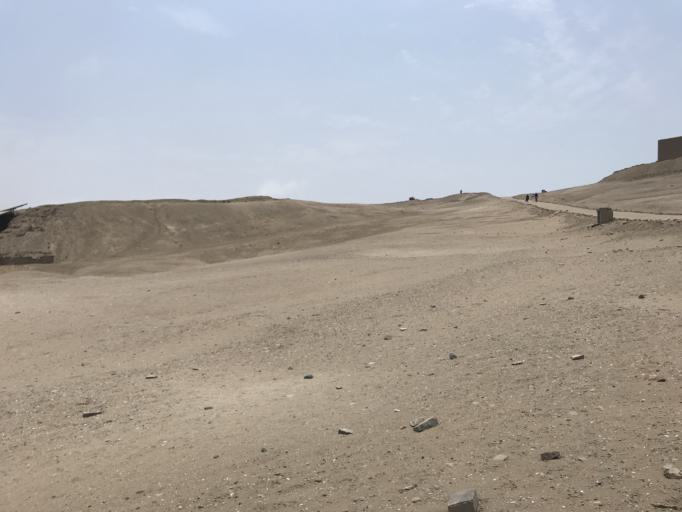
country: PE
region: Lima
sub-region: Lima
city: Punta Hermosa
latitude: -12.2606
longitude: -76.9024
